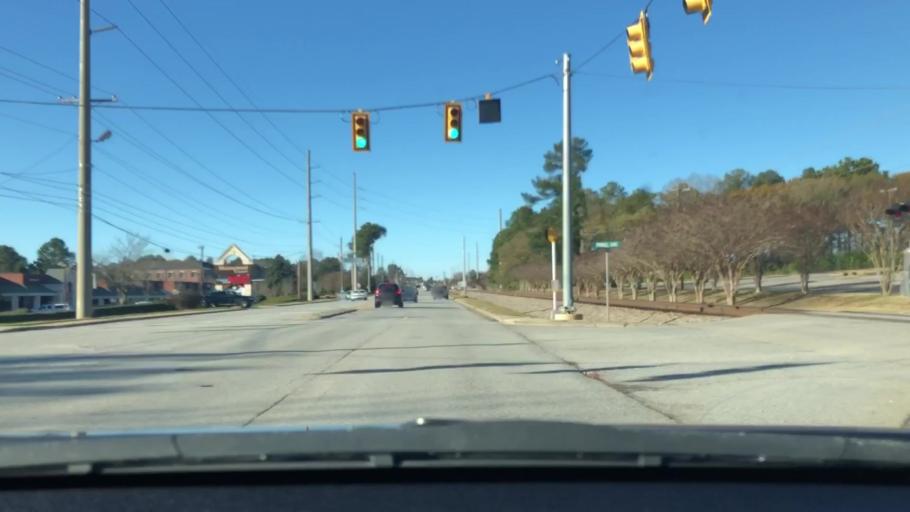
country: US
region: South Carolina
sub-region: Lexington County
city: Irmo
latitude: 34.0750
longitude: -81.1770
